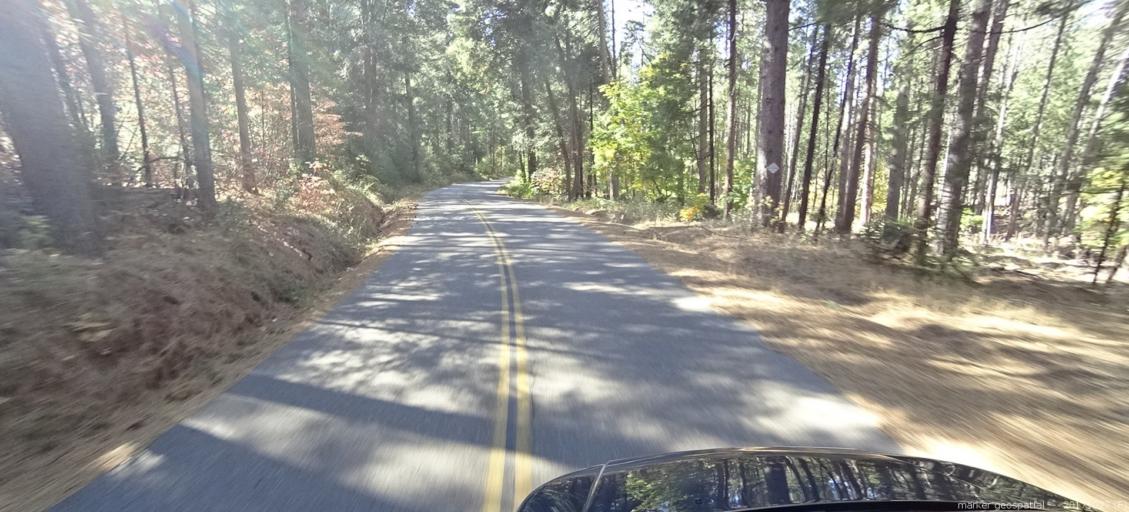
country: US
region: California
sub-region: Shasta County
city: Shingletown
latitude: 40.7419
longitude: -121.9333
